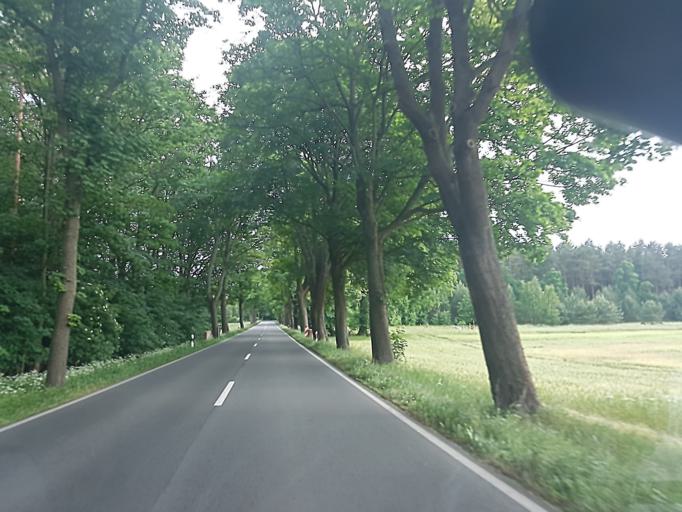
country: DE
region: Saxony-Anhalt
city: Nudersdorf
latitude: 51.9252
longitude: 12.6047
